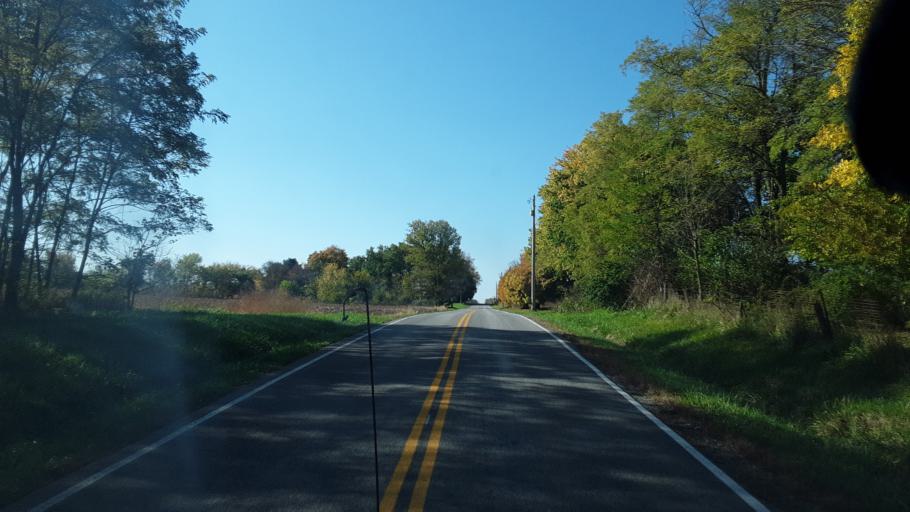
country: US
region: Ohio
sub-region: Highland County
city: Leesburg
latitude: 39.2671
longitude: -83.5452
